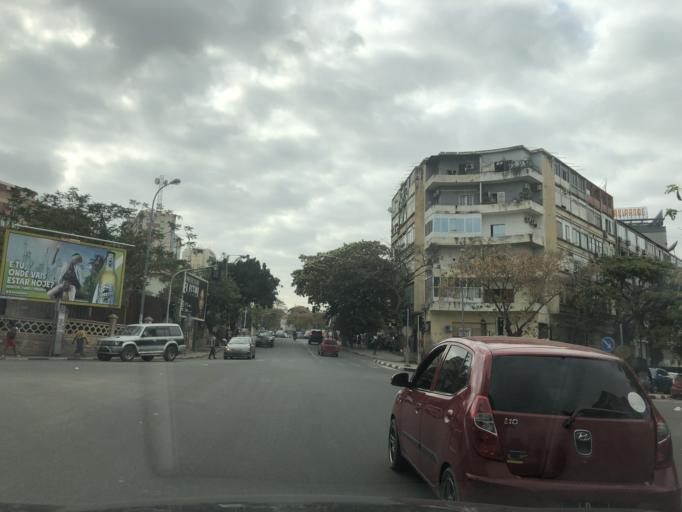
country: AO
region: Luanda
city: Luanda
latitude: -8.8233
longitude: 13.2298
